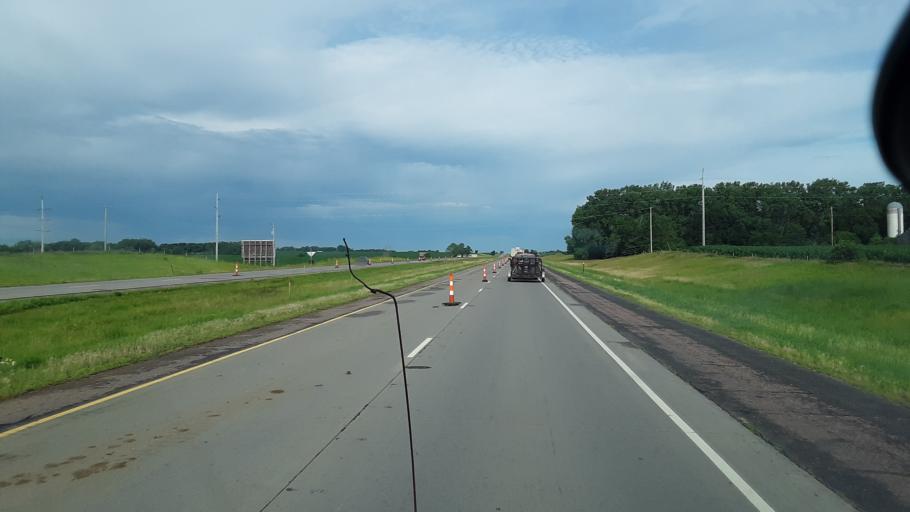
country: US
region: South Dakota
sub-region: Minnehaha County
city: Crooks
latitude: 43.6088
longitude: -96.8286
